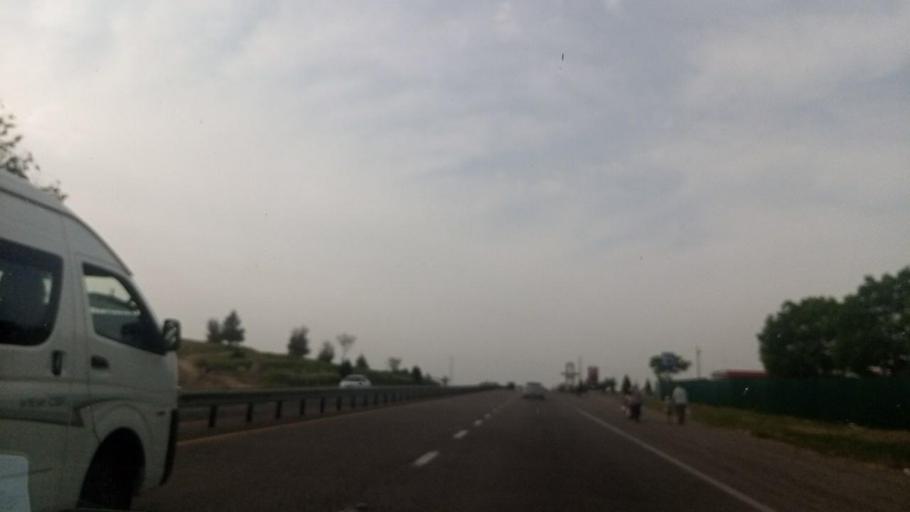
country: UZ
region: Toshkent
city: Tuytepa
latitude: 41.1210
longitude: 69.4417
